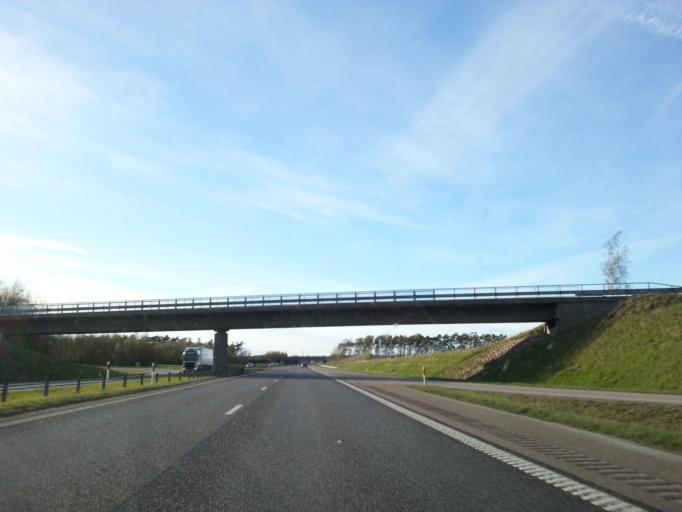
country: SE
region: Halland
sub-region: Laholms Kommun
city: Mellbystrand
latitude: 56.4523
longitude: 12.9486
